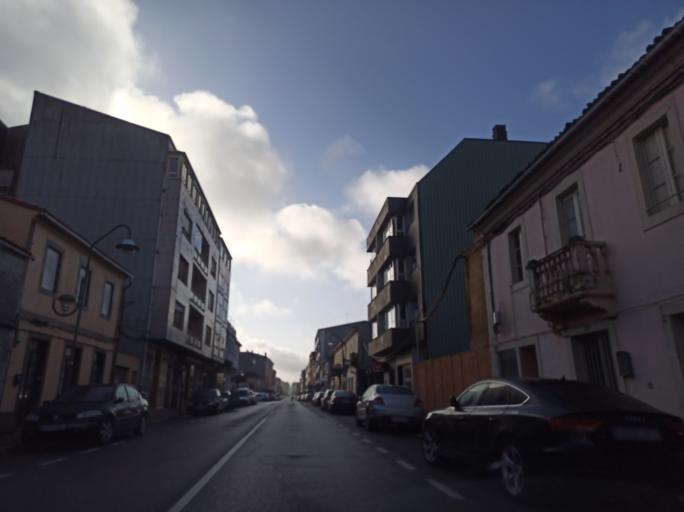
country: ES
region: Galicia
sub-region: Provincia da Coruna
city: Curtis
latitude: 43.1398
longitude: -8.0366
